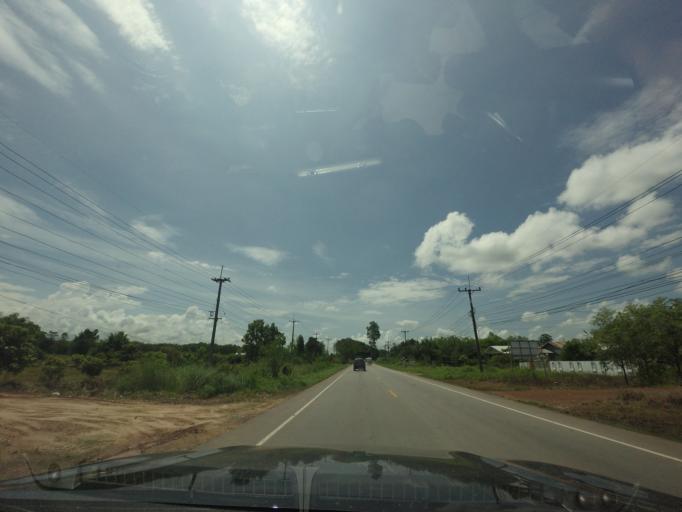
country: TH
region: Changwat Udon Thani
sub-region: Amphoe Ban Phue
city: Ban Phue
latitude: 17.7268
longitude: 102.3949
